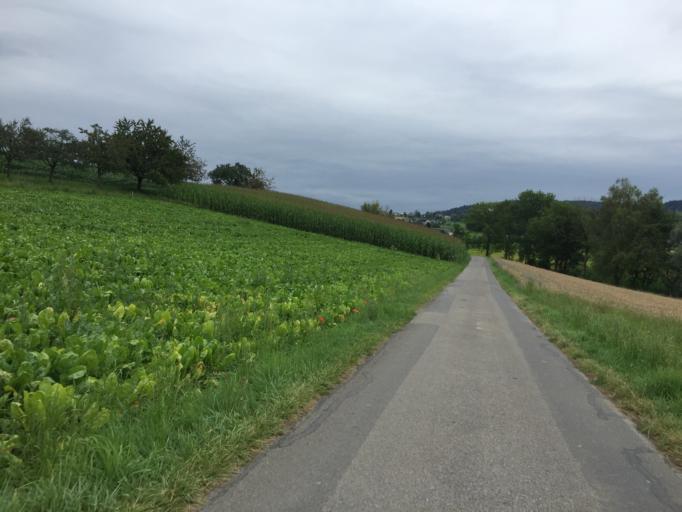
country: CH
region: Bern
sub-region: Bern-Mittelland District
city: Worb
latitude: 46.9172
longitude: 7.5902
